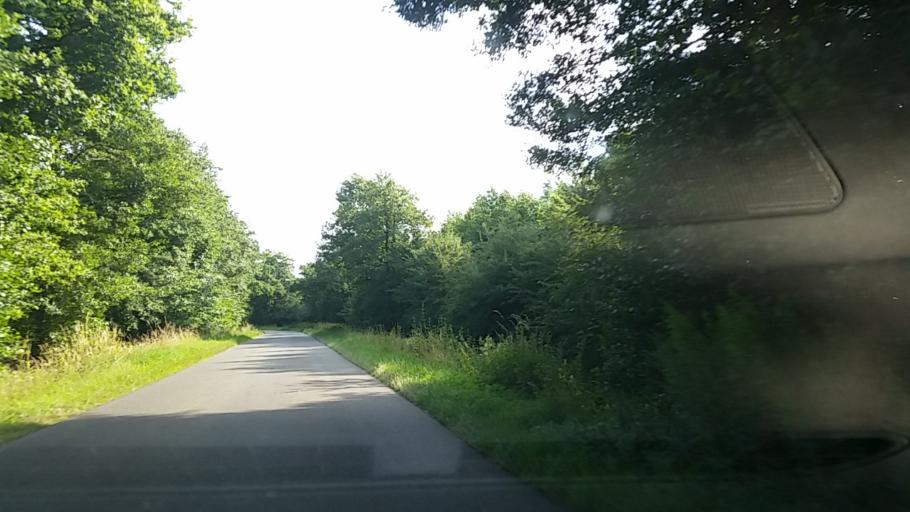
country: DE
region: Lower Saxony
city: Radbruch
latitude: 53.3258
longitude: 10.2435
